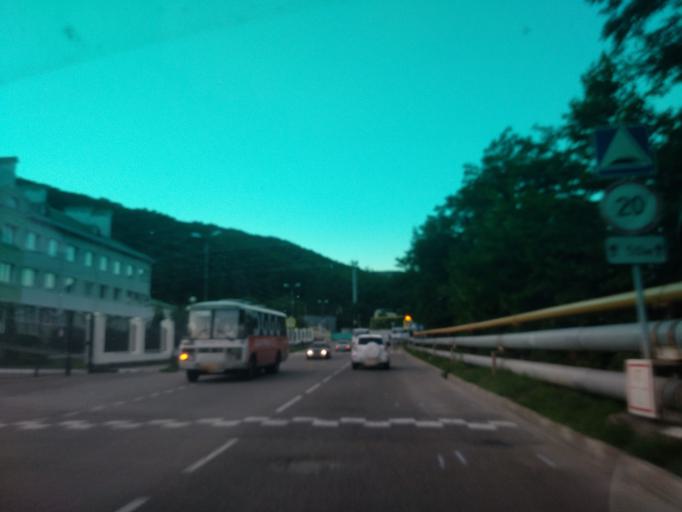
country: RU
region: Krasnodarskiy
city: Tuapse
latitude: 44.1200
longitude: 39.0699
